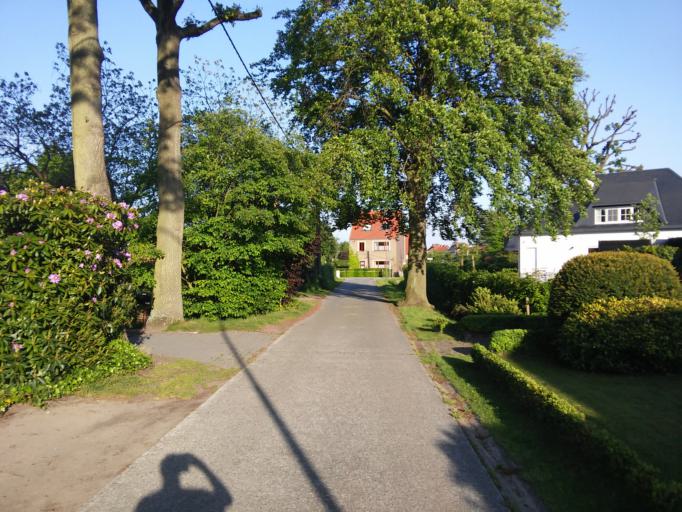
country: BE
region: Flanders
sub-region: Provincie Antwerpen
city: Duffel
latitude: 51.0718
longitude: 4.4827
